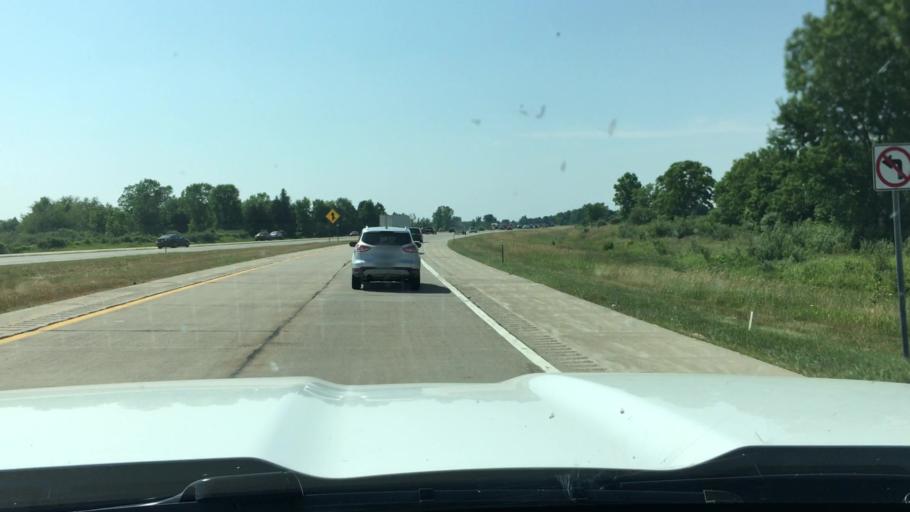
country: US
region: Michigan
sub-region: Clinton County
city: Wacousta
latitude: 42.7905
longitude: -84.6769
